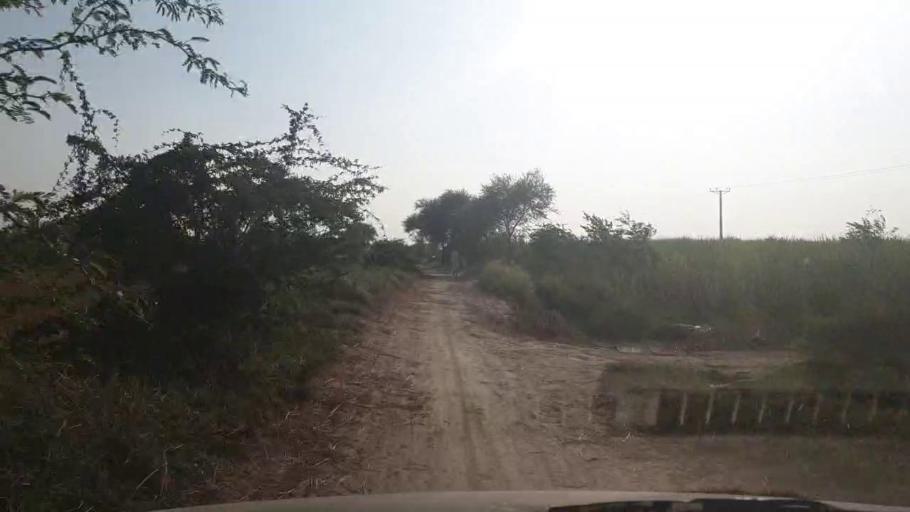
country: PK
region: Sindh
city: Badin
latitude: 24.6332
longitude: 68.7975
